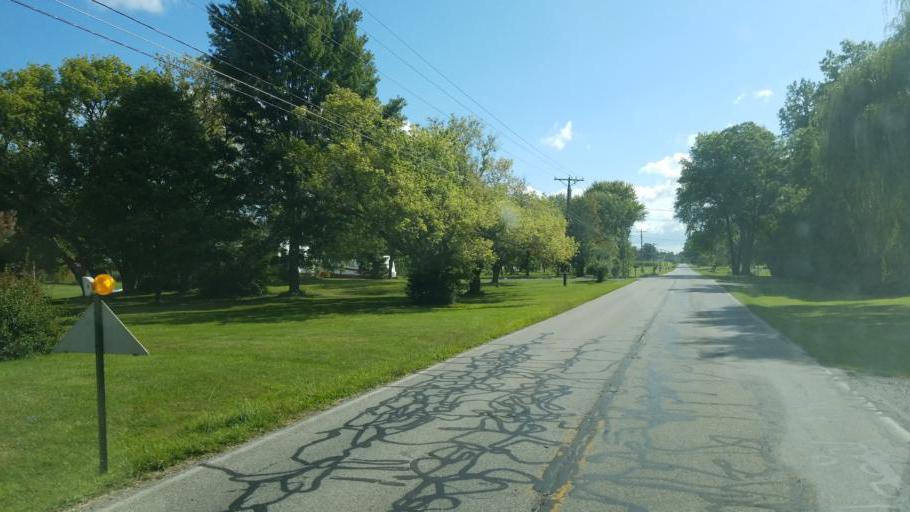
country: US
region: Ohio
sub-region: Lorain County
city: Oberlin
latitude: 41.2794
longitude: -82.2001
